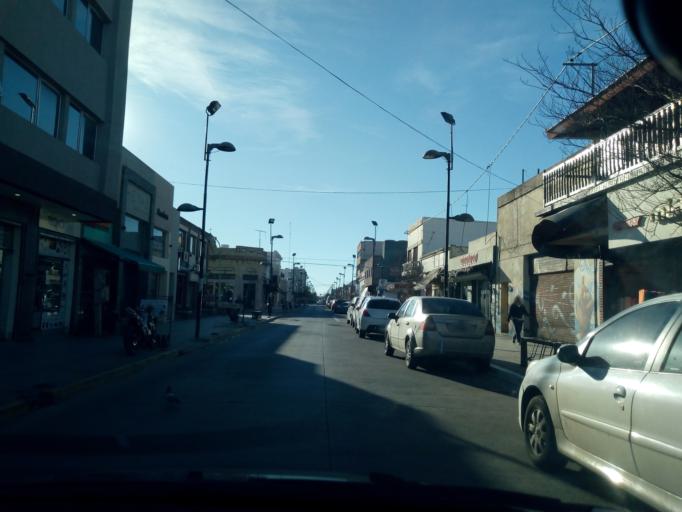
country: AR
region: Buenos Aires
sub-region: Partido de Ensenada
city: Ensenada
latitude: -34.8592
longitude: -57.9049
